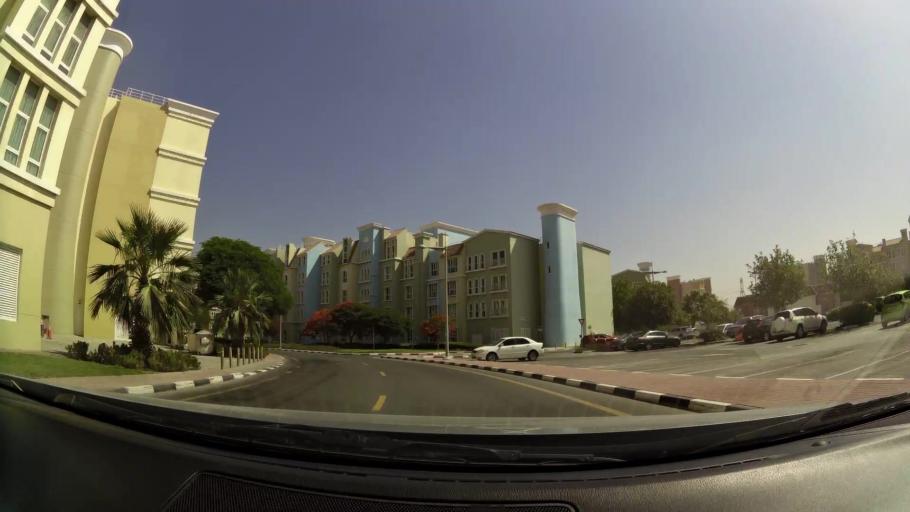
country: AE
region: Dubai
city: Dubai
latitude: 25.0294
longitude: 55.1562
